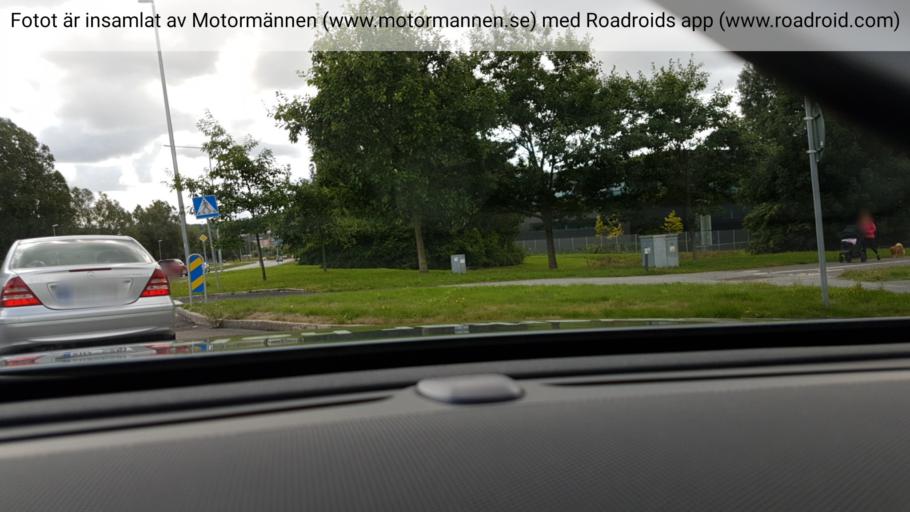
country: SE
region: Vaestra Goetaland
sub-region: Molndal
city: Moelndal
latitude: 57.6504
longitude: 11.9878
